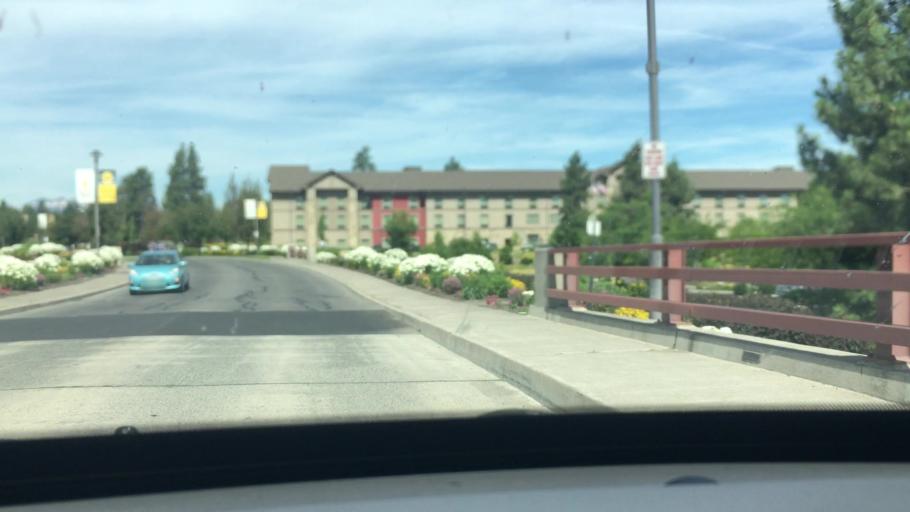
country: US
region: Oregon
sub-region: Deschutes County
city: Bend
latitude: 44.0434
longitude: -121.3166
